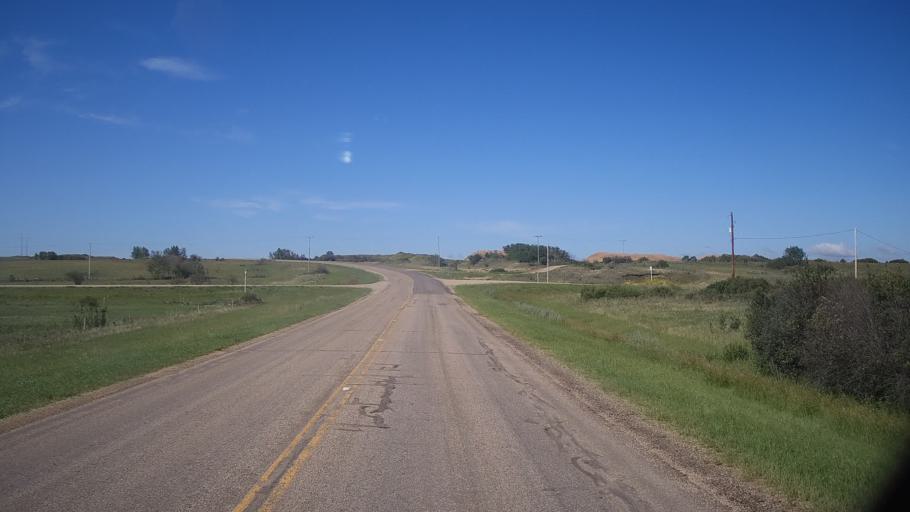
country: CA
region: Saskatchewan
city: Watrous
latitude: 51.7085
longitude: -105.3773
